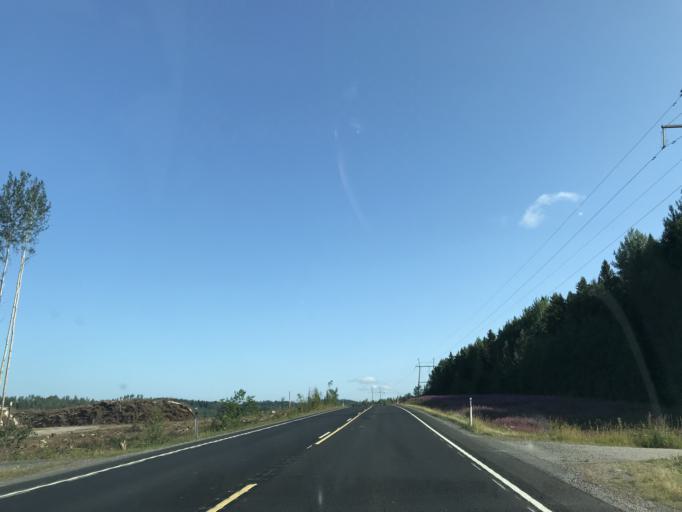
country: FI
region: Paijanne Tavastia
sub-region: Lahti
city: Lahti
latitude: 61.1140
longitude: 25.6418
